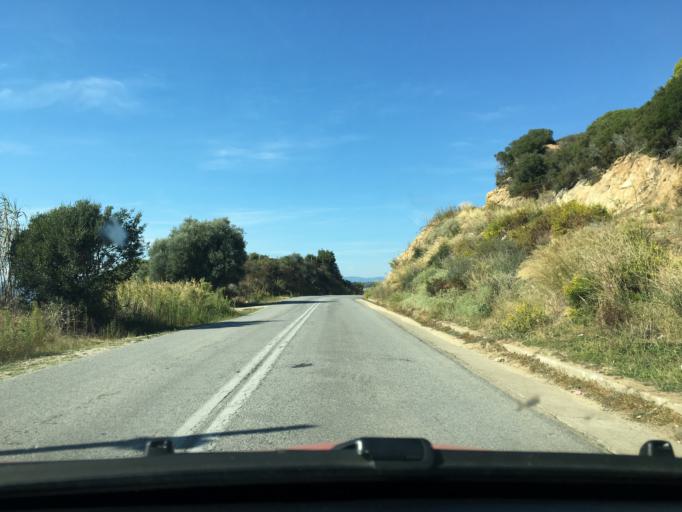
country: GR
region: Central Macedonia
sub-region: Nomos Chalkidikis
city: Ouranoupolis
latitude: 40.3332
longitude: 23.9737
